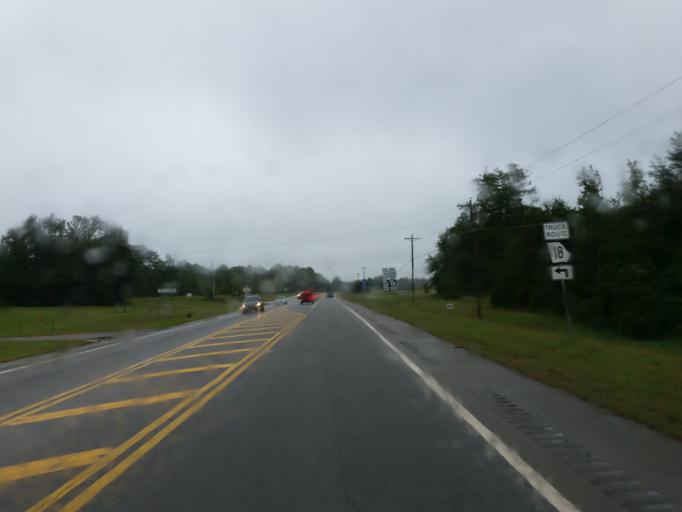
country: US
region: Georgia
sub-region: Lamar County
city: Barnesville
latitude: 33.0315
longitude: -84.1466
